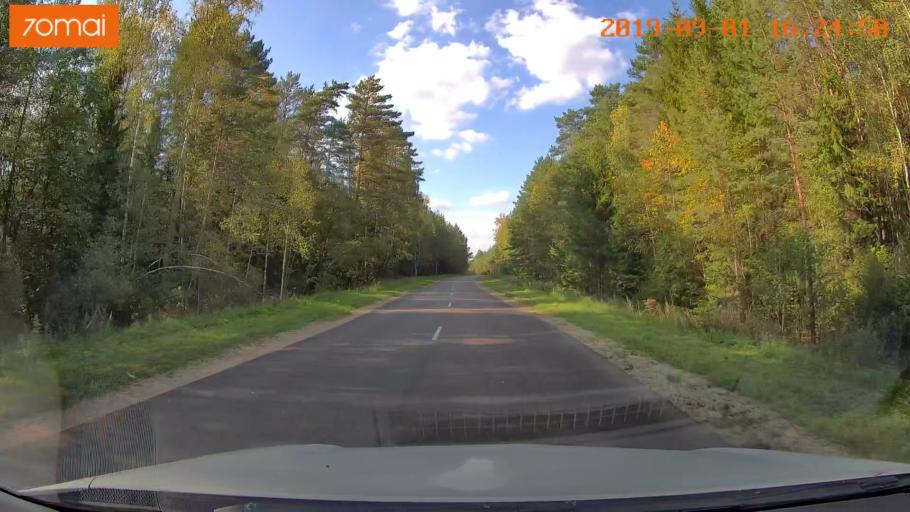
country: RU
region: Kaluga
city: Maloyaroslavets
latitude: 54.8954
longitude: 36.5195
